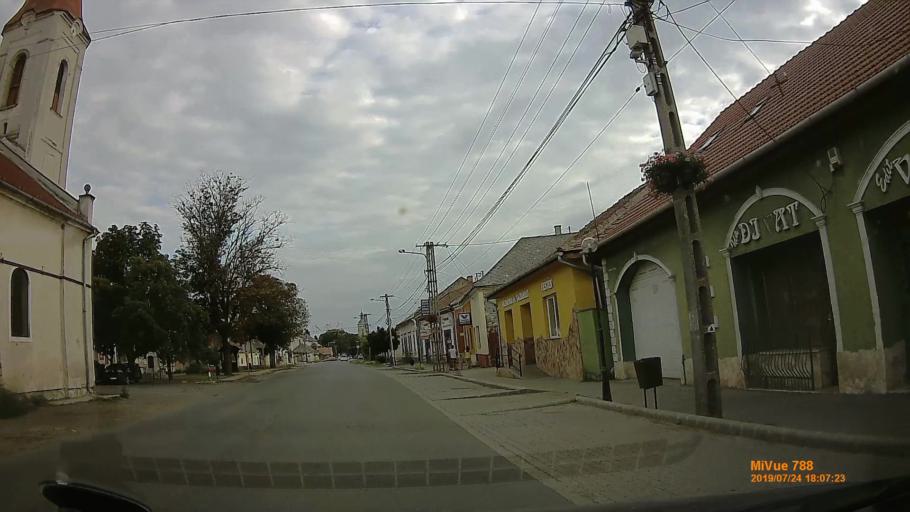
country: HU
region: Borsod-Abauj-Zemplen
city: Abaujszanto
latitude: 48.2806
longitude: 21.1867
